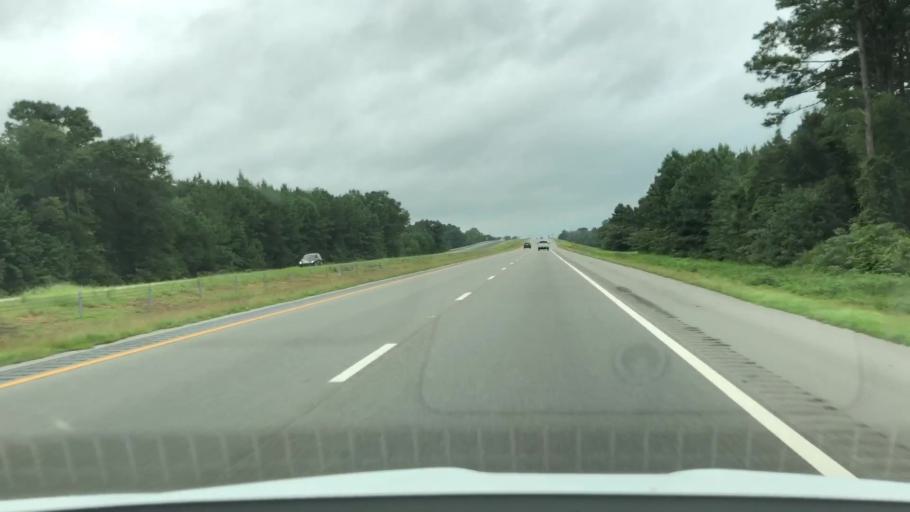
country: US
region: North Carolina
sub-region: Lenoir County
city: La Grange
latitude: 35.3367
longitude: -77.8438
